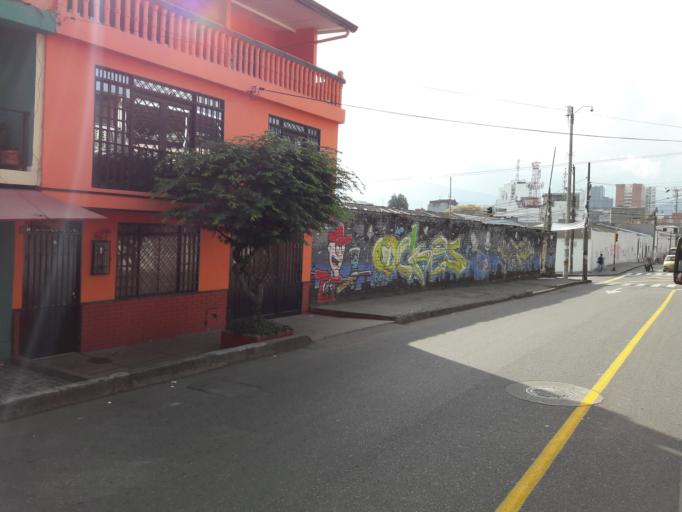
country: CO
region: Tolima
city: Ibague
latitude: 4.4362
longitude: -75.2115
